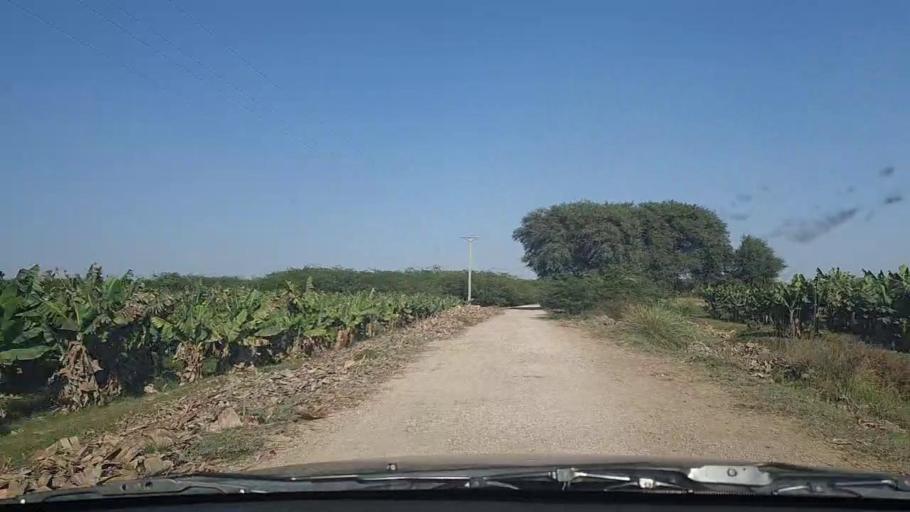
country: PK
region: Sindh
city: Chuhar Jamali
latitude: 24.3238
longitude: 67.7590
